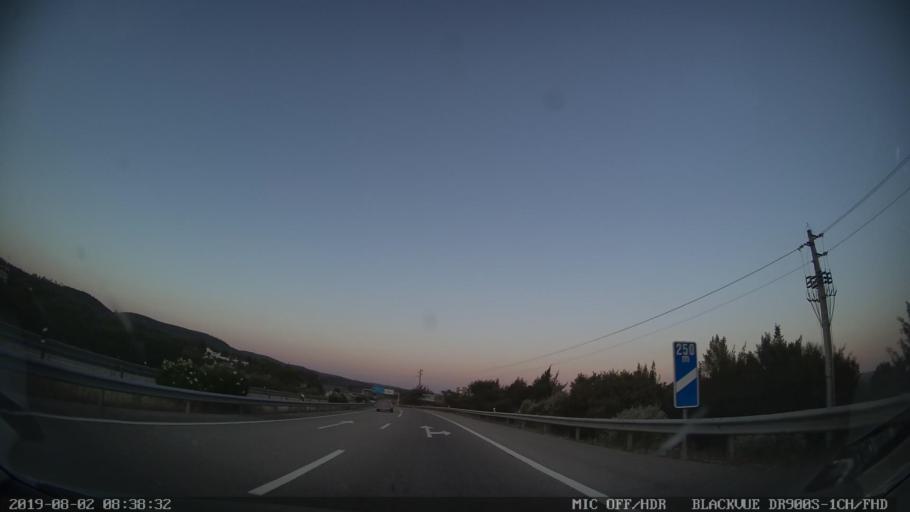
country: PT
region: Santarem
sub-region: Constancia
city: Constancia
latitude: 39.4841
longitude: -8.3324
